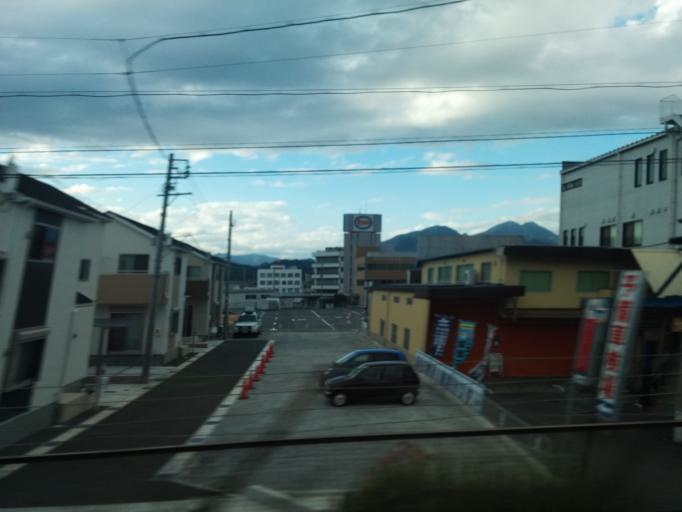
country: JP
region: Shizuoka
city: Shizuoka-shi
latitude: 34.9955
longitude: 138.4299
